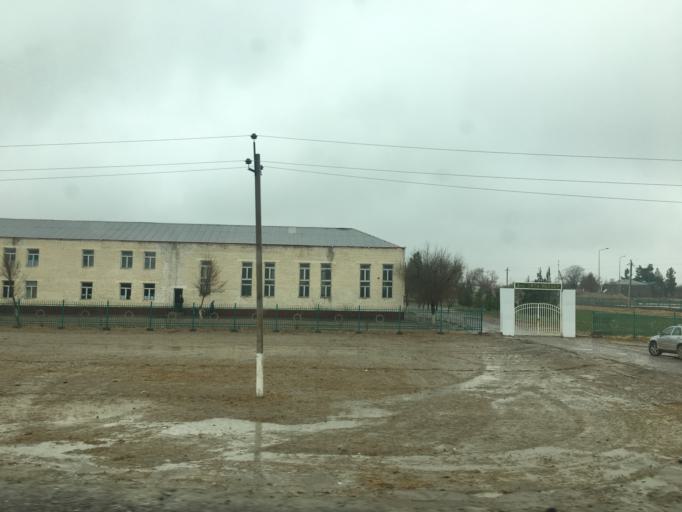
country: TM
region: Mary
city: Yoloeten
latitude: 37.3276
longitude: 62.3010
